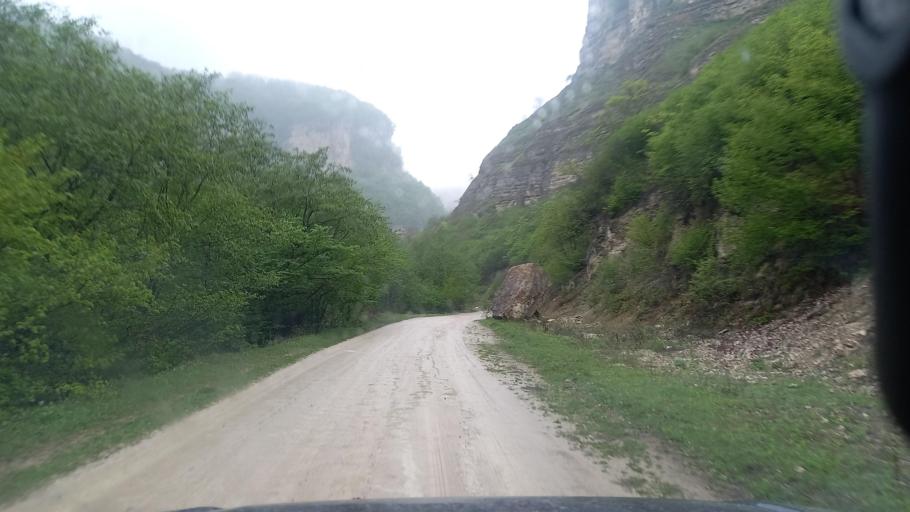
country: RU
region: Kabardino-Balkariya
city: Gundelen
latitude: 43.5937
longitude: 43.1328
